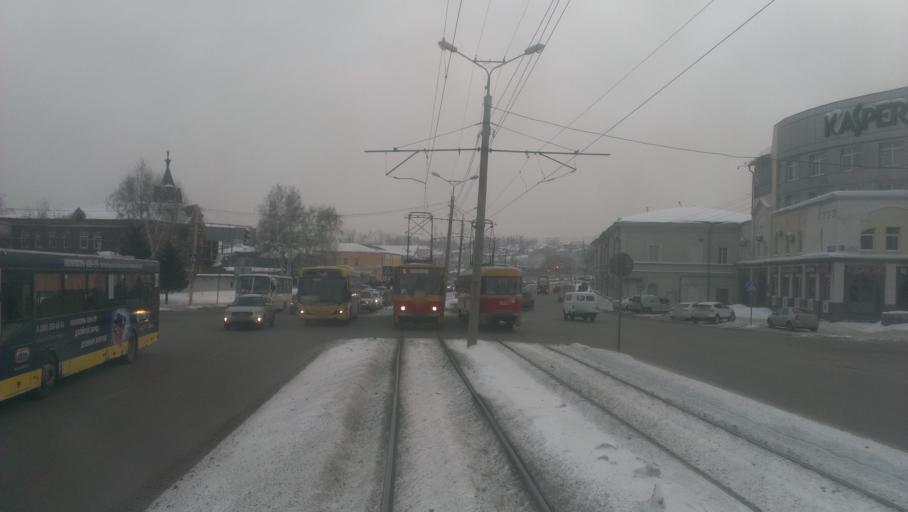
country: RU
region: Altai Krai
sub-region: Gorod Barnaulskiy
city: Barnaul
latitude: 53.3306
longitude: 83.7826
